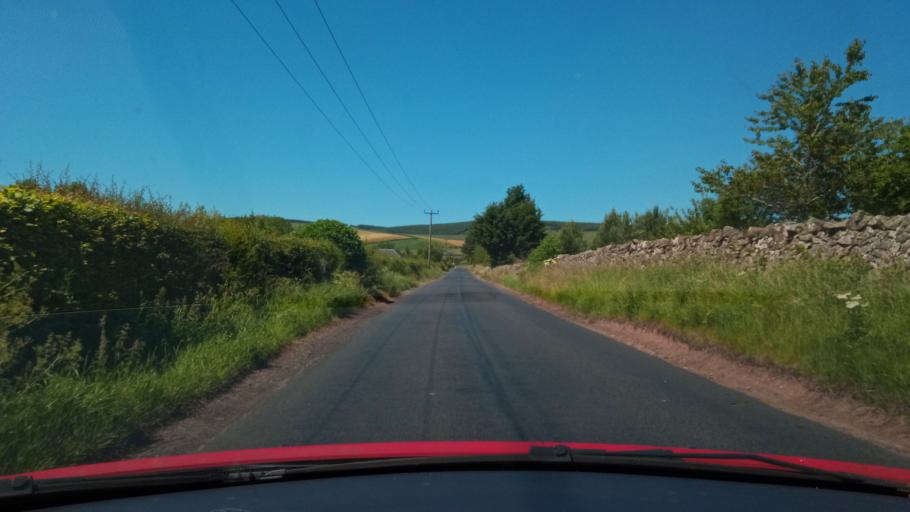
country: GB
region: Scotland
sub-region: The Scottish Borders
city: Duns
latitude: 55.7754
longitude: -2.3750
